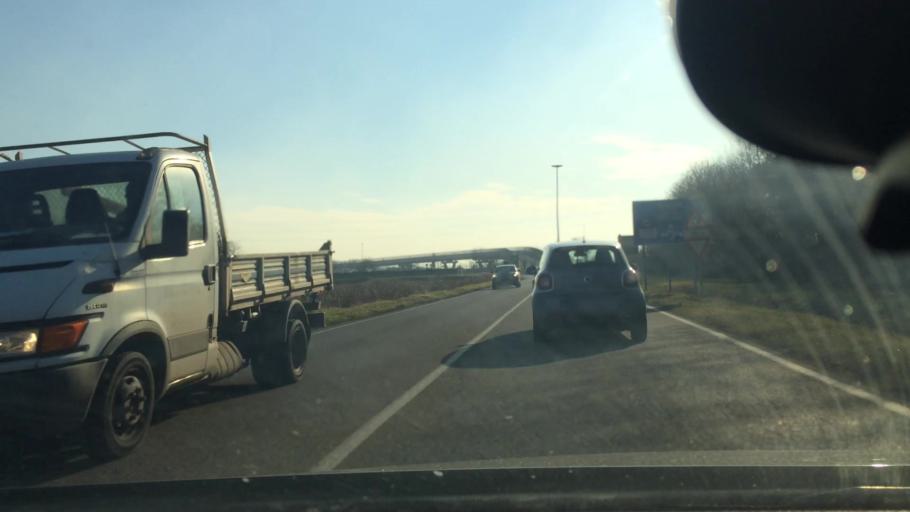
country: IT
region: Lombardy
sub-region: Citta metropolitana di Milano
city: Arluno
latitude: 45.5038
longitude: 8.9297
